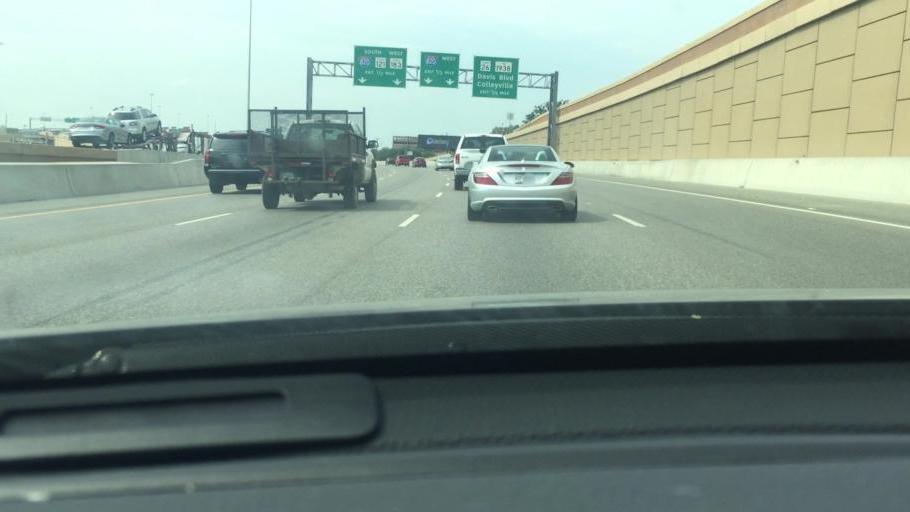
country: US
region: Texas
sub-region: Tarrant County
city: Hurst
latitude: 32.8386
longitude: -97.1924
